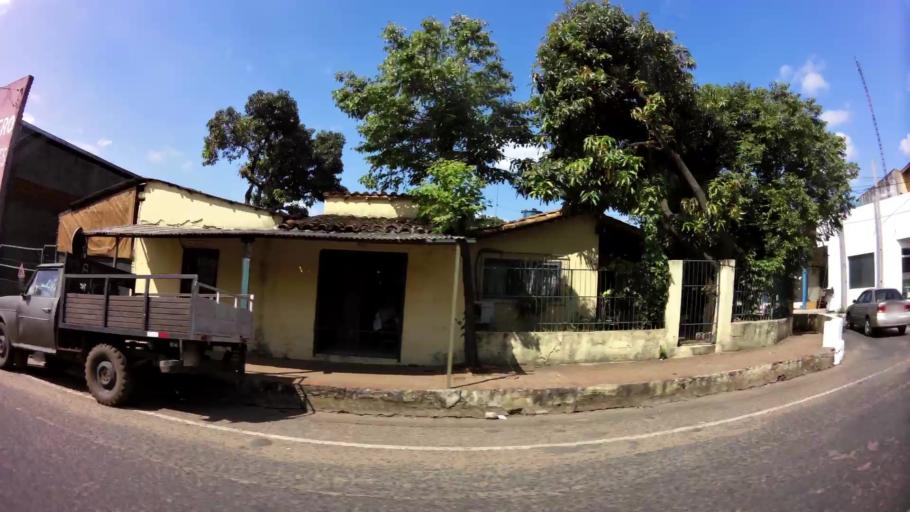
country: PY
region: Central
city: Fernando de la Mora
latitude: -25.3438
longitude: -57.5171
